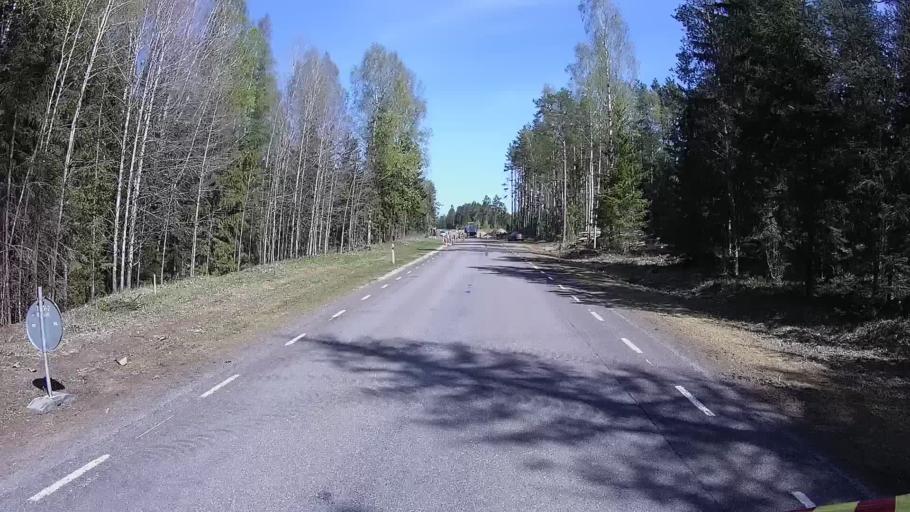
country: EE
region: Harju
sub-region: Nissi vald
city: Turba
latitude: 59.1086
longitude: 24.0438
